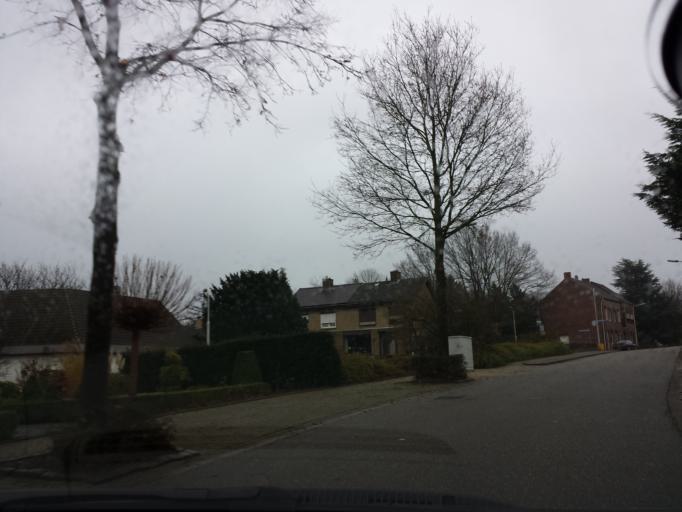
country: NL
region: Limburg
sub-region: Gemeente Kerkrade
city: Kerkrade
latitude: 50.8808
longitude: 6.0691
